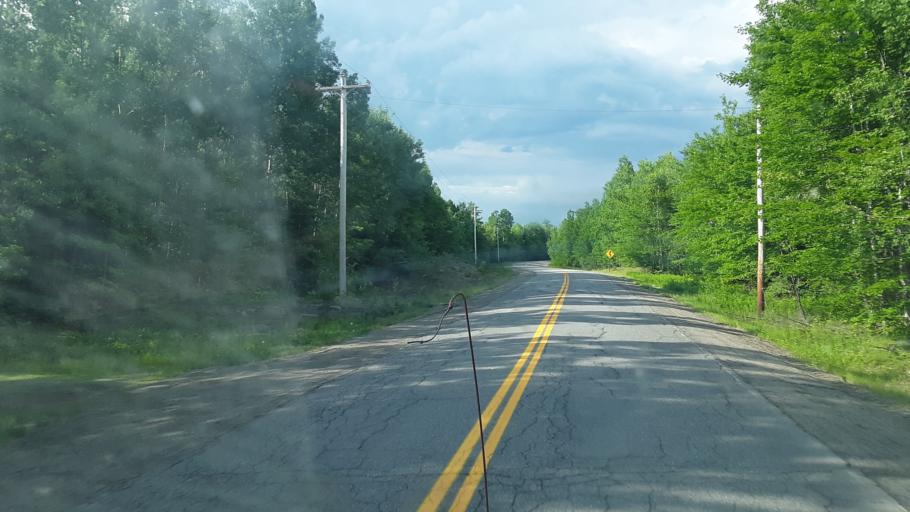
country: US
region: Maine
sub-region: Washington County
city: Calais
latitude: 45.1111
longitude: -67.5073
